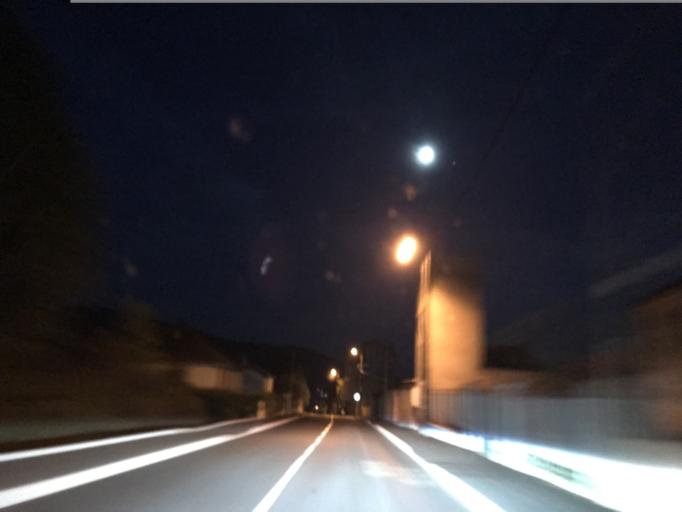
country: FR
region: Auvergne
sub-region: Departement du Puy-de-Dome
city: Thiers
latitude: 45.8605
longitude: 3.5319
